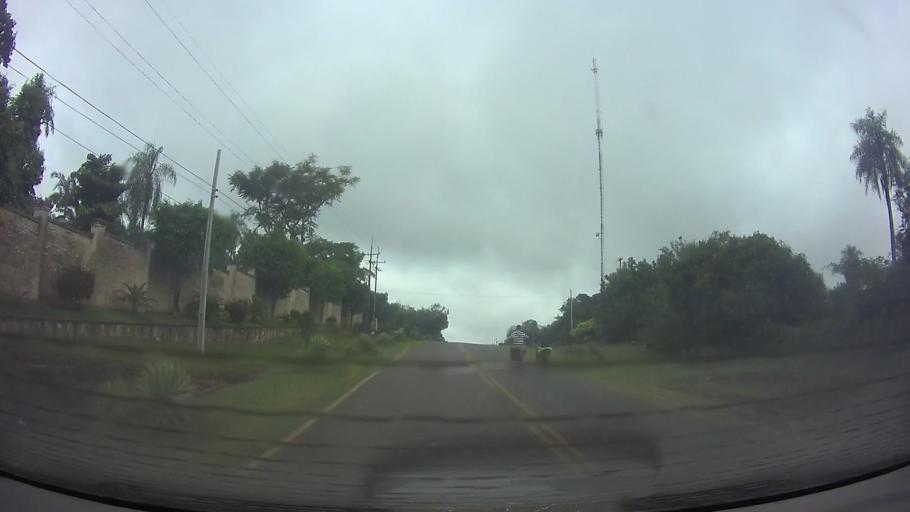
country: PY
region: Cordillera
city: Altos
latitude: -25.2673
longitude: -57.2420
